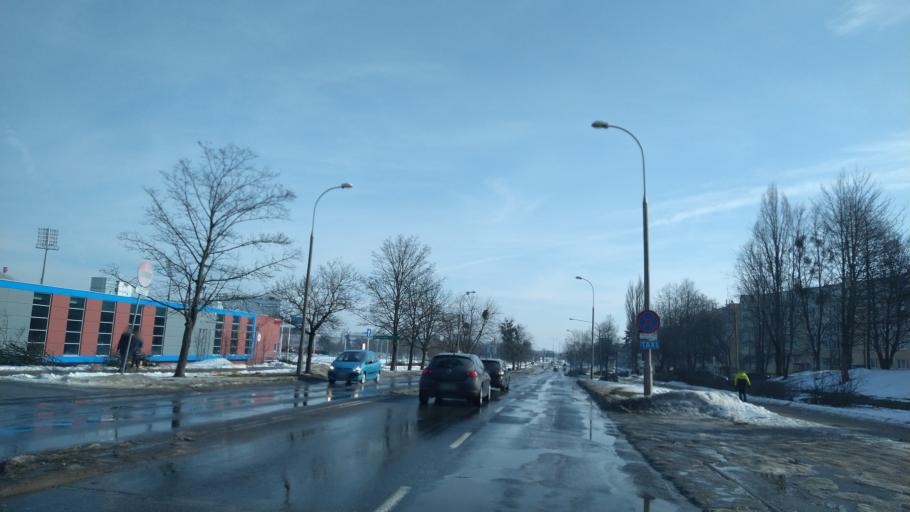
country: PL
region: Warmian-Masurian Voivodeship
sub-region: Powiat olsztynski
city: Olsztyn
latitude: 53.7719
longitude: 20.5042
